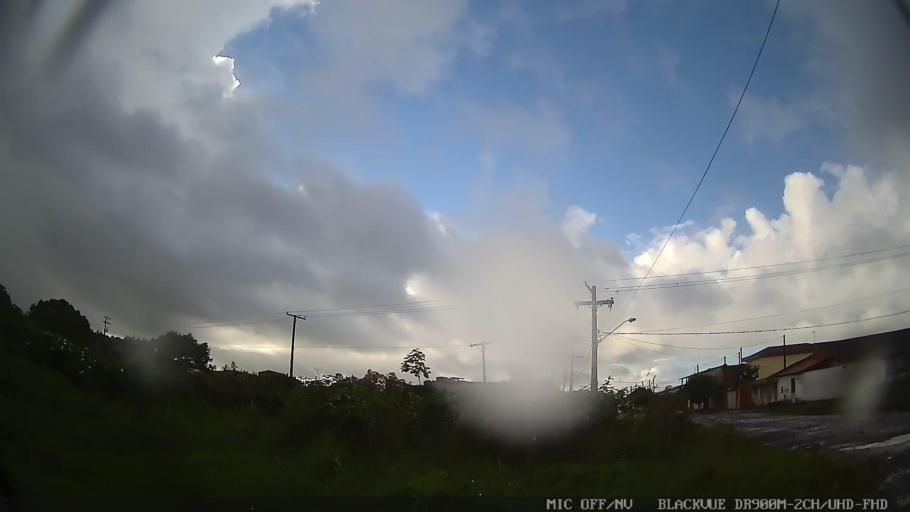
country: BR
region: Sao Paulo
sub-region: Itanhaem
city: Itanhaem
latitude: -24.2390
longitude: -46.9003
